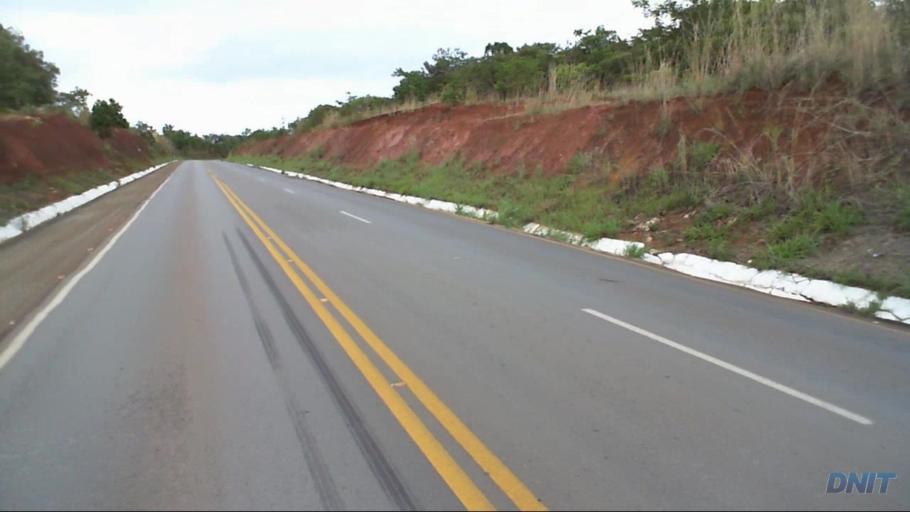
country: BR
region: Goias
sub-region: Barro Alto
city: Barro Alto
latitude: -14.8680
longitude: -49.0110
